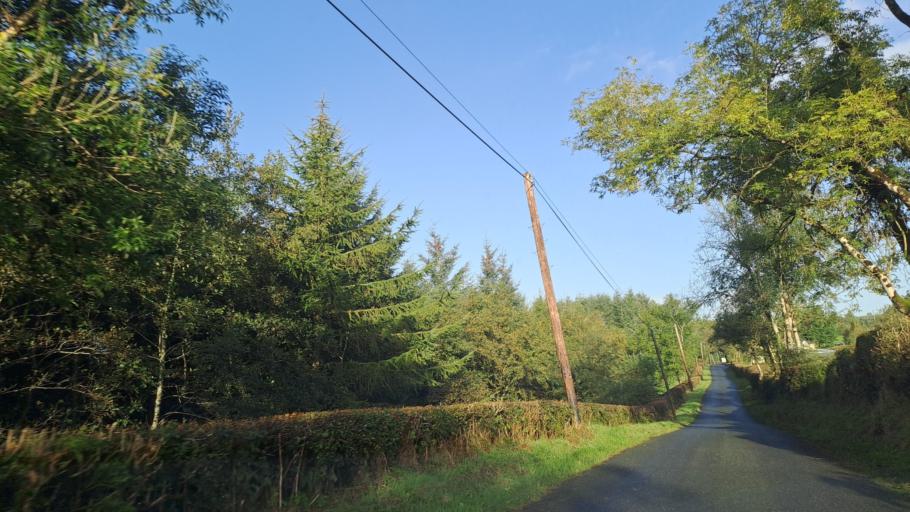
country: IE
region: Ulster
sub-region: County Monaghan
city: Castleblayney
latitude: 54.0692
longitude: -6.8315
